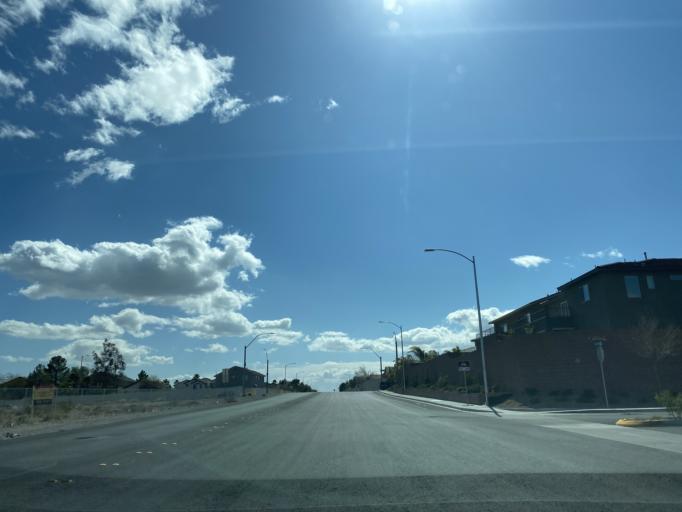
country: US
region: Nevada
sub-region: Clark County
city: Summerlin South
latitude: 36.2345
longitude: -115.3065
